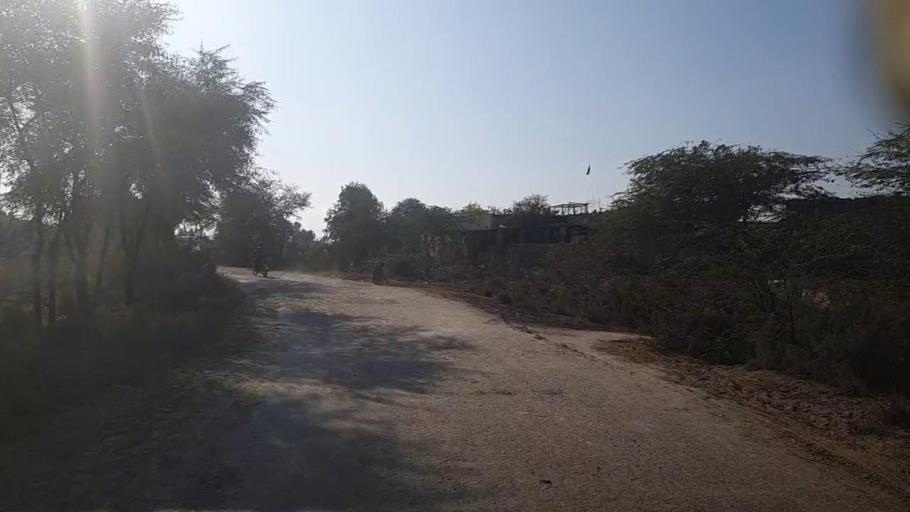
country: PK
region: Sindh
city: Khairpur
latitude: 28.0632
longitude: 69.6924
